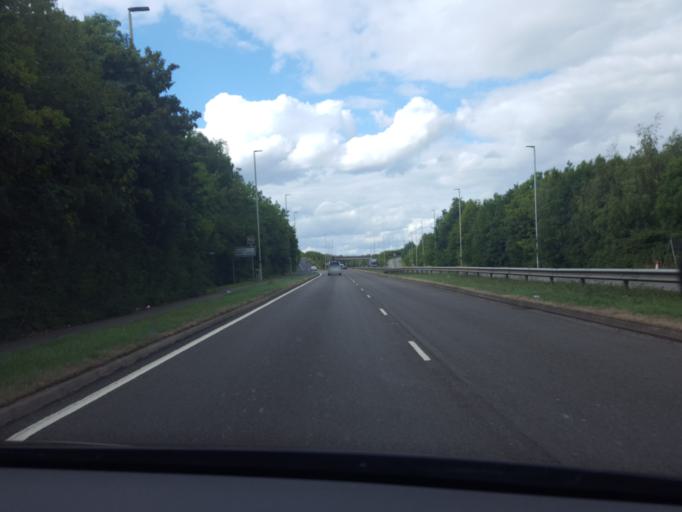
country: GB
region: England
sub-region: Leicestershire
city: Enderby
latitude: 52.6098
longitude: -1.1896
